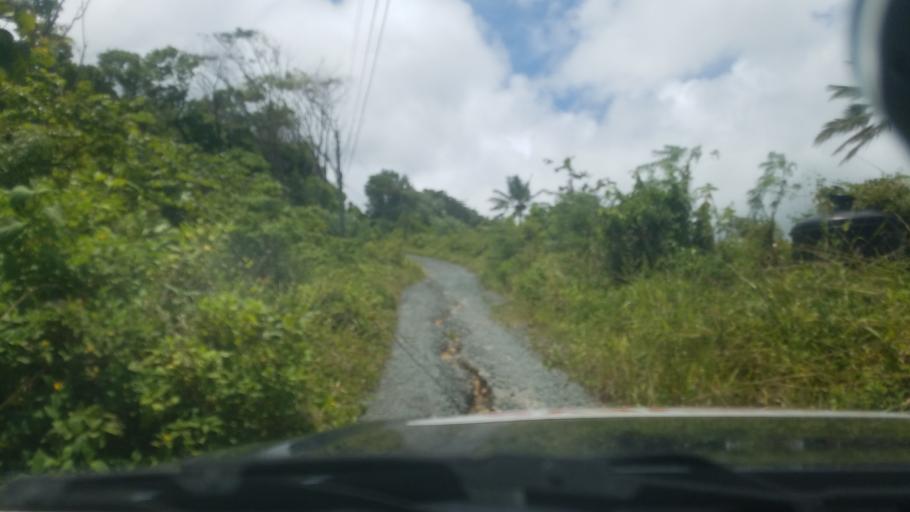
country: LC
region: Praslin
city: Praslin
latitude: 13.8726
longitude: -60.9143
